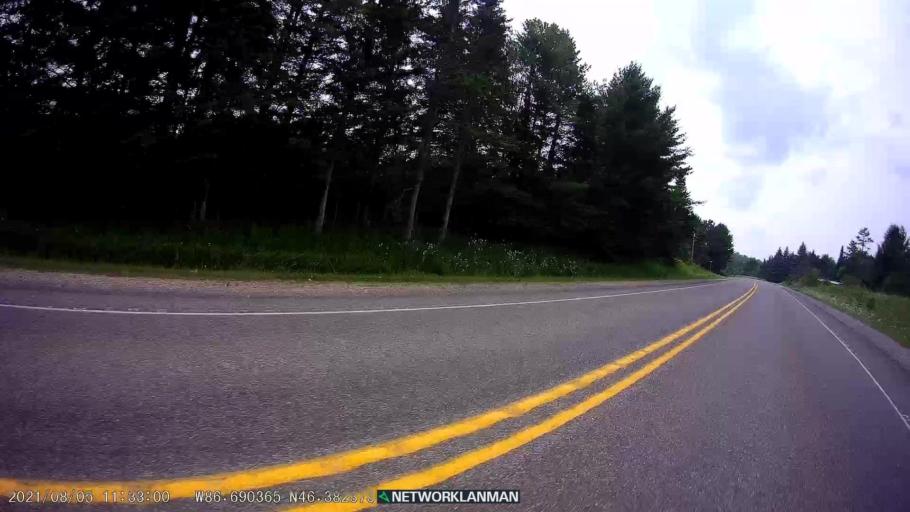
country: US
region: Michigan
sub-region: Alger County
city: Munising
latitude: 46.3823
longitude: -86.6905
